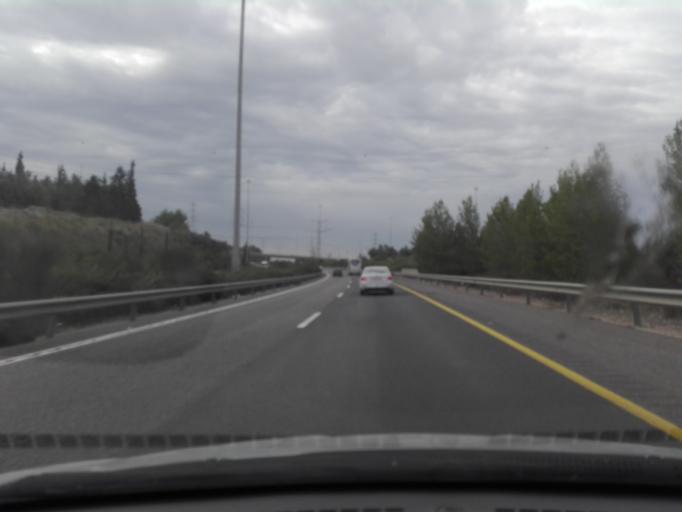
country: IL
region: Central District
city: Lod
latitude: 31.9593
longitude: 34.9378
